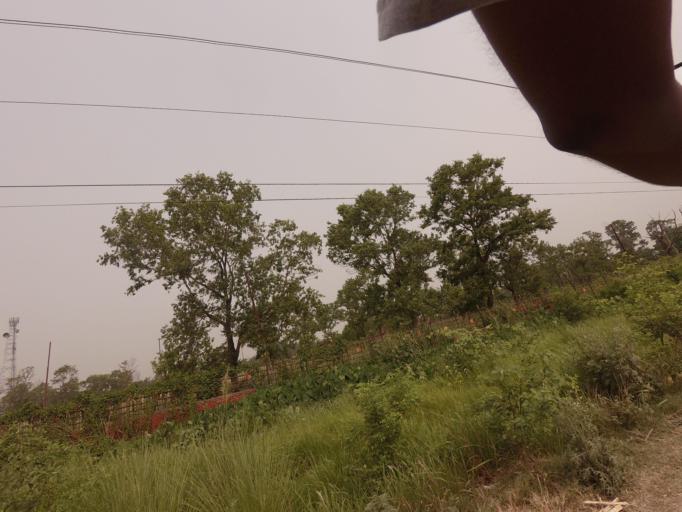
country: IN
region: Uttar Pradesh
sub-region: Maharajganj
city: Nautanwa
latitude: 27.4938
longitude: 83.2844
